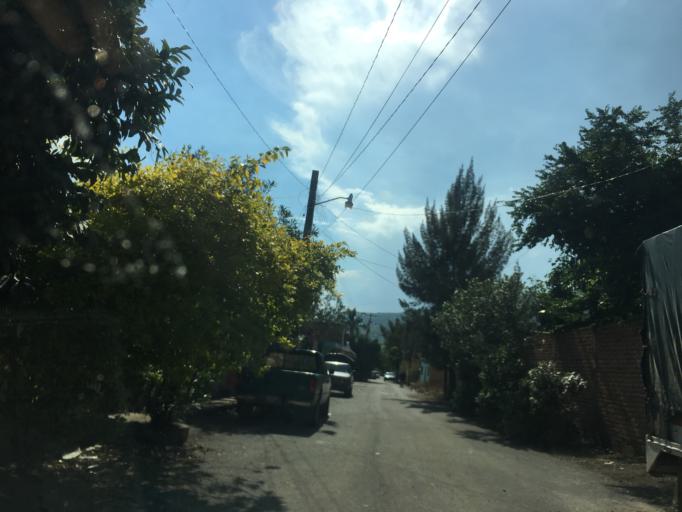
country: MX
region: Nayarit
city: Ixtlan del Rio
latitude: 21.0427
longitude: -104.3612
